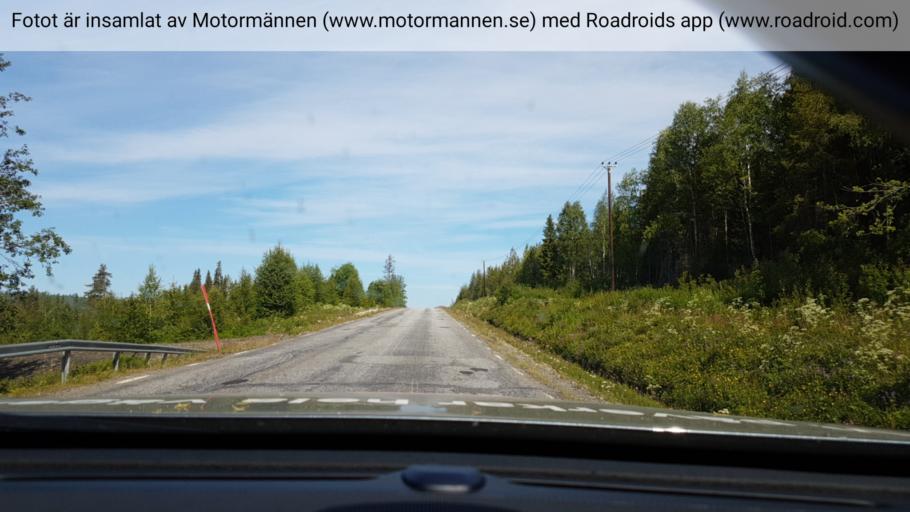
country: SE
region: Vaesterbotten
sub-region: Vilhelmina Kommun
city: Sjoberg
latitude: 64.5321
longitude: 15.8945
